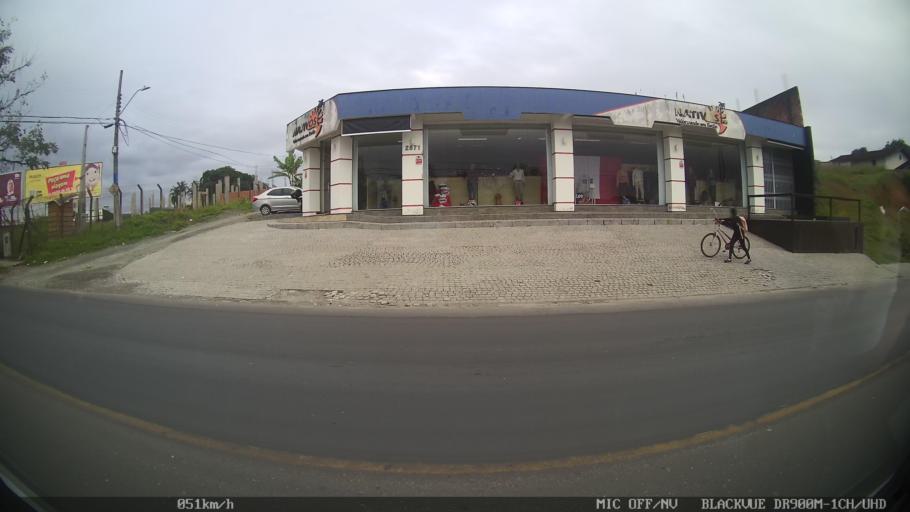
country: BR
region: Santa Catarina
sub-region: Joinville
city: Joinville
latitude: -26.2851
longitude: -48.8743
